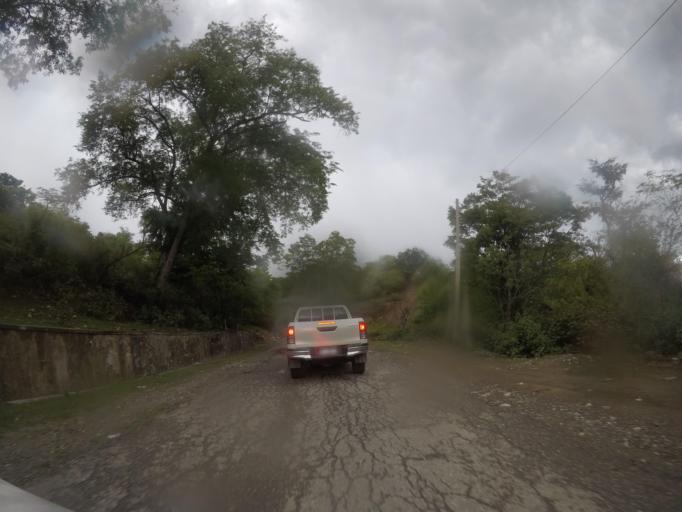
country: ID
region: East Nusa Tenggara
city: Atambua
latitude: -8.9643
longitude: 125.0064
